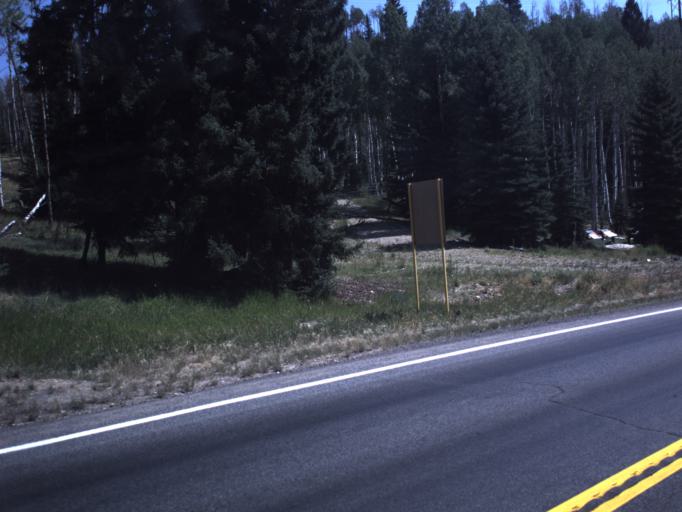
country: US
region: Utah
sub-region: Sanpete County
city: Fairview
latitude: 39.6858
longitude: -111.1602
